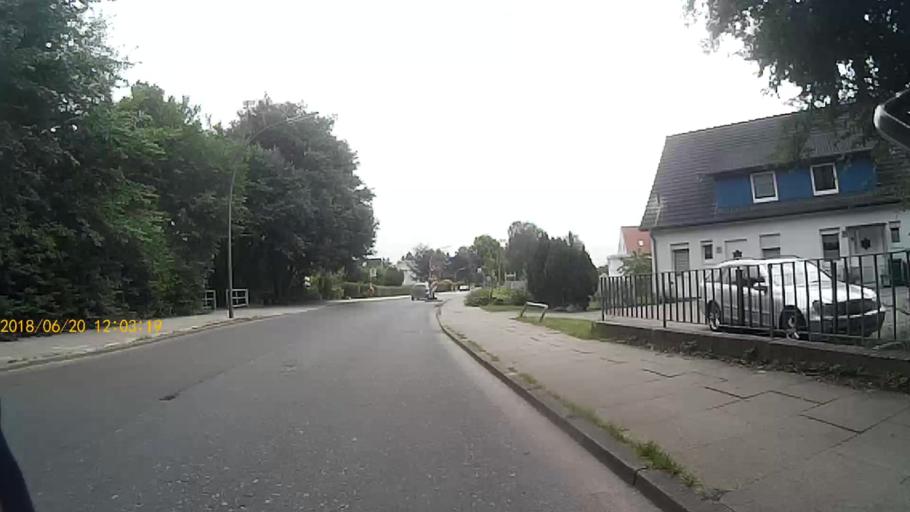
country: DE
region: Hamburg
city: Kleiner Grasbrook
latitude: 53.4971
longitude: 10.0142
